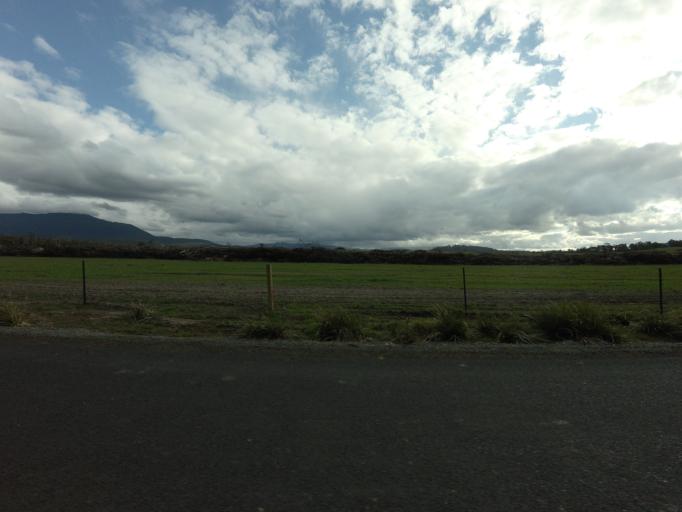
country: AU
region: Tasmania
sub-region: Northern Midlands
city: Longford
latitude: -41.8482
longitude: 147.2145
